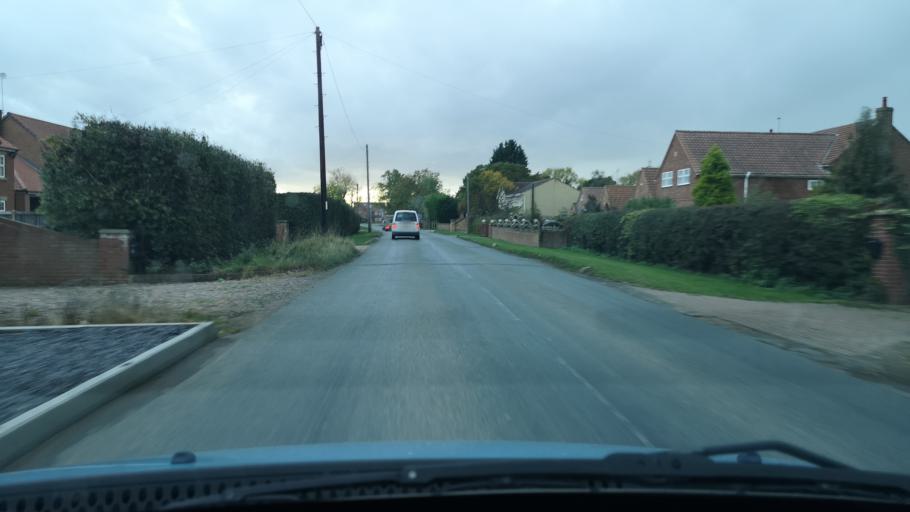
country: GB
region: England
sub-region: Doncaster
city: Moss
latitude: 53.6226
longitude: -1.0933
